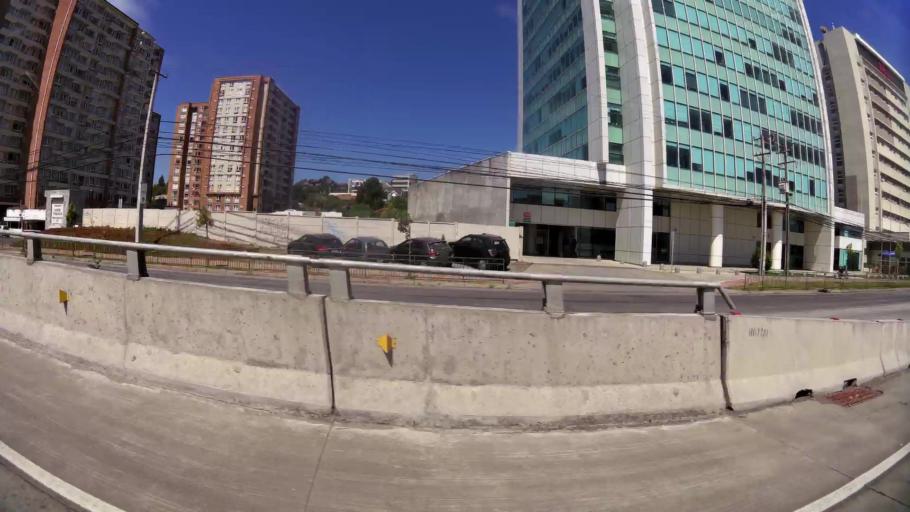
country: CL
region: Biobio
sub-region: Provincia de Concepcion
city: Concepcion
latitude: -36.7913
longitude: -73.0629
